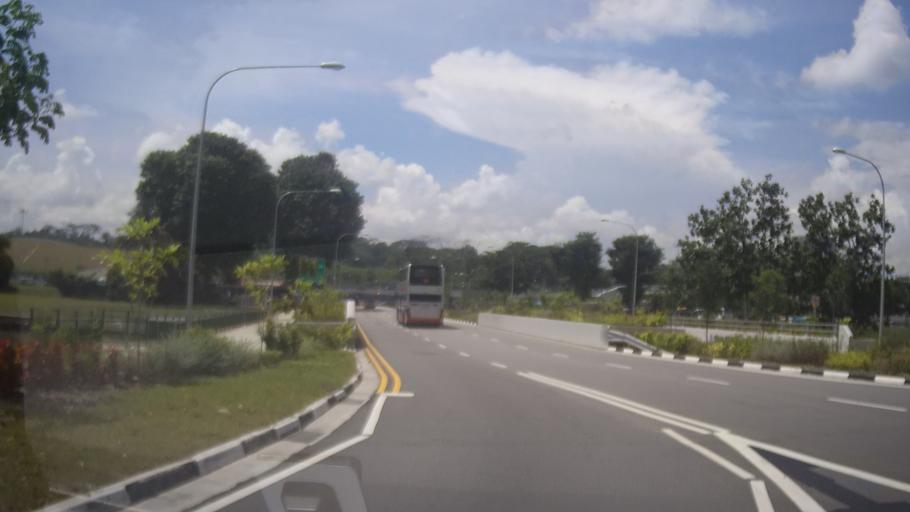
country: MY
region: Johor
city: Johor Bahru
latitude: 1.3945
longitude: 103.7522
